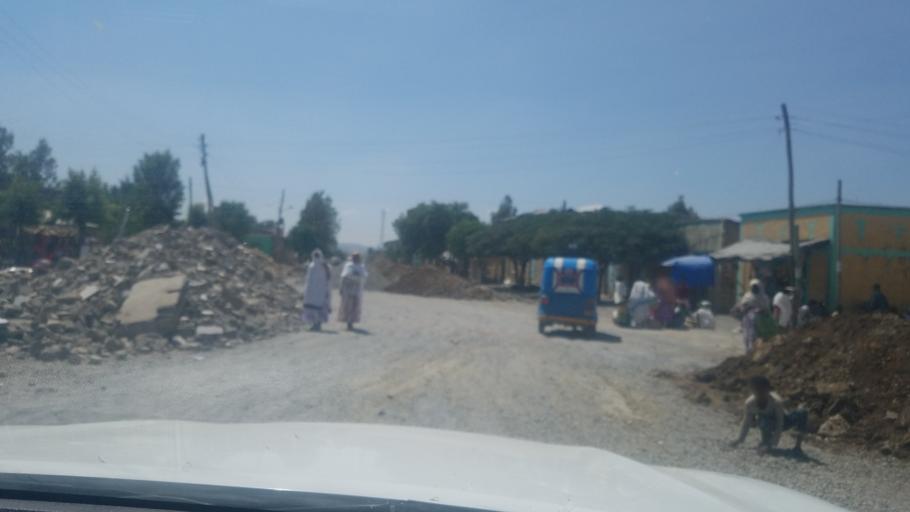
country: ET
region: Tigray
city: Mekele
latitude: 13.7936
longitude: 39.5993
